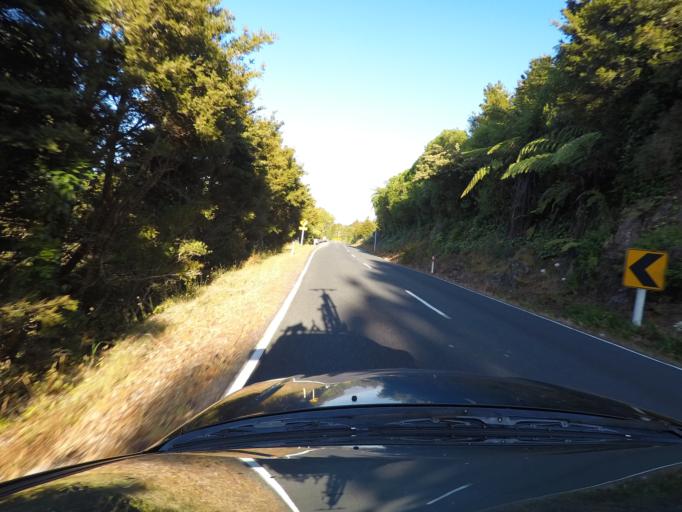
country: NZ
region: Northland
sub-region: Whangarei
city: Whangarei
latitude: -35.6563
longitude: 174.3121
